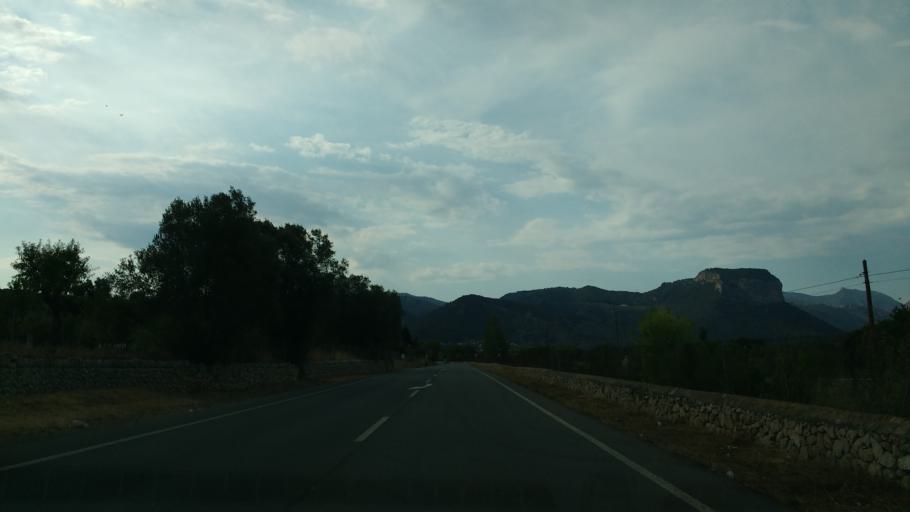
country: ES
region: Balearic Islands
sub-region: Illes Balears
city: Consell
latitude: 39.6877
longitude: 2.8075
